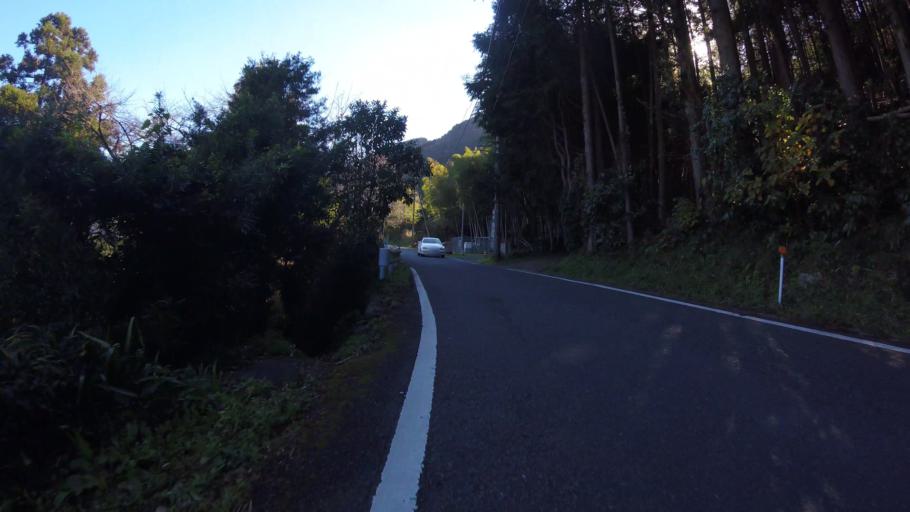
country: JP
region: Shizuoka
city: Shimoda
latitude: 34.7679
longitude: 138.9608
